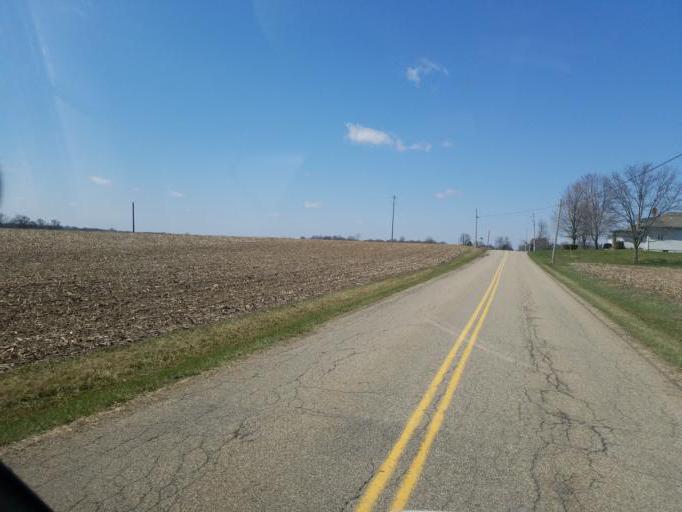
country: US
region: Ohio
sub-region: Knox County
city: Centerburg
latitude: 40.2956
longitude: -82.6684
